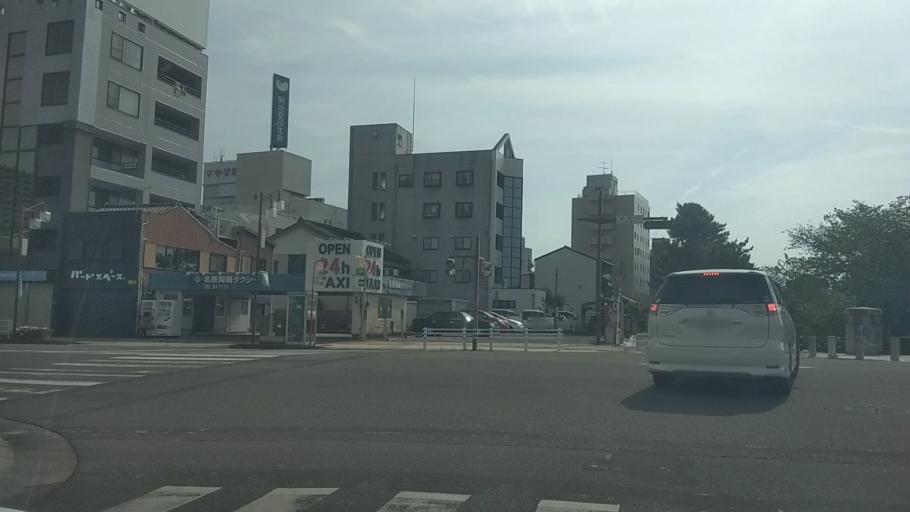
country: JP
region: Aichi
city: Okazaki
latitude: 34.9559
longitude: 137.1637
